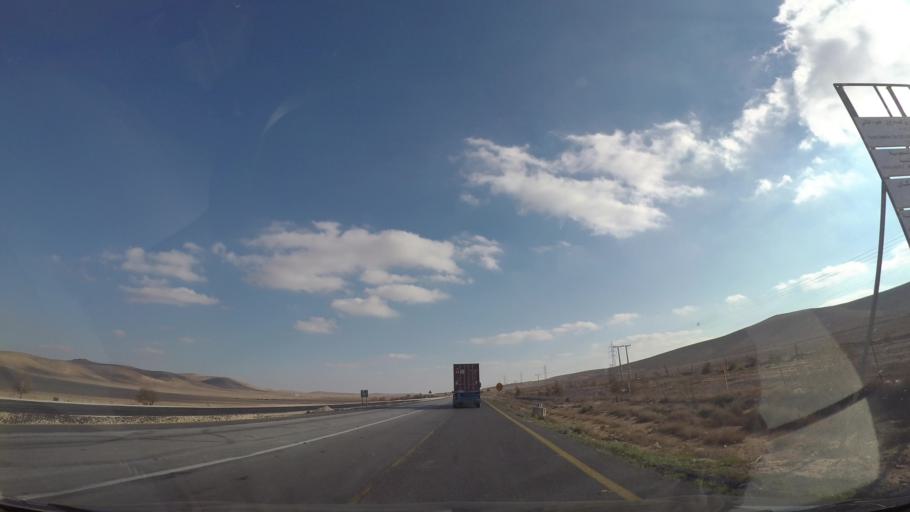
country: JO
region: Karak
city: Karak City
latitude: 31.1857
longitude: 36.0187
